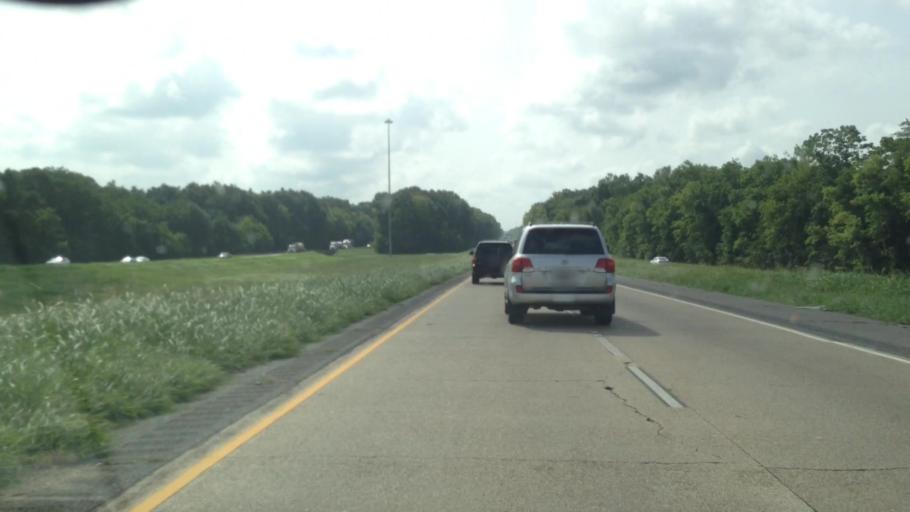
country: US
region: Louisiana
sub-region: Ascension Parish
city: Gonzales
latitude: 30.1914
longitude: -90.9188
